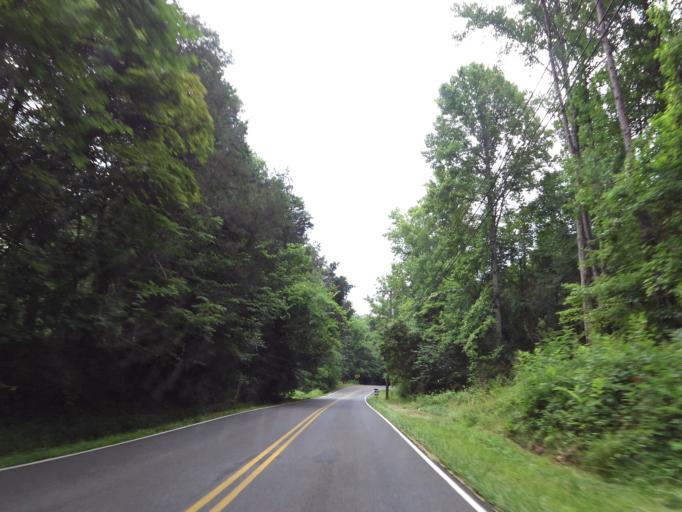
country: US
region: Tennessee
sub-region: Knox County
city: Knoxville
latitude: 35.9228
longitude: -83.8534
